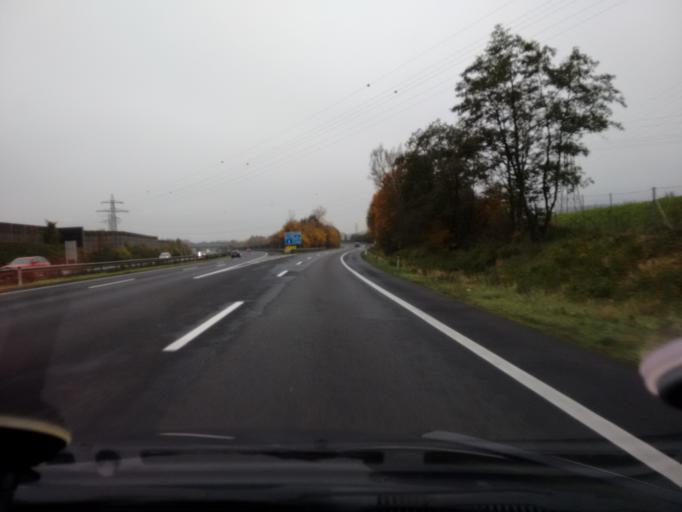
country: AT
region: Upper Austria
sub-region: Wels Stadt
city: Wels
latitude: 48.1816
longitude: 14.0033
